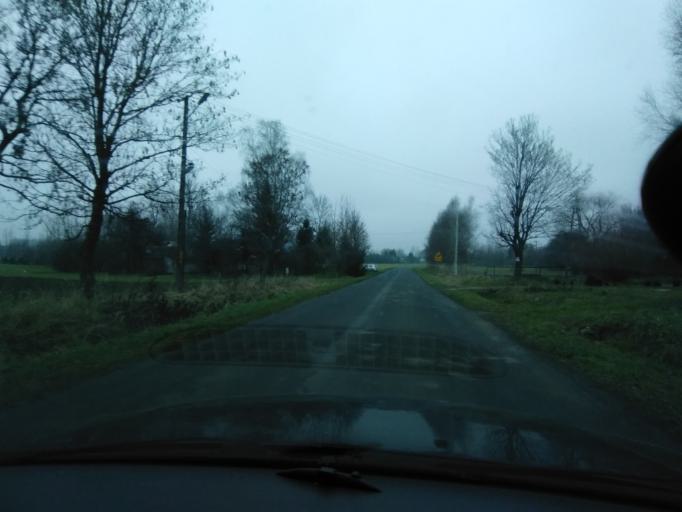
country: PL
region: Subcarpathian Voivodeship
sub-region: Powiat przeworski
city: Zarzecze
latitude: 49.9520
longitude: 22.5681
